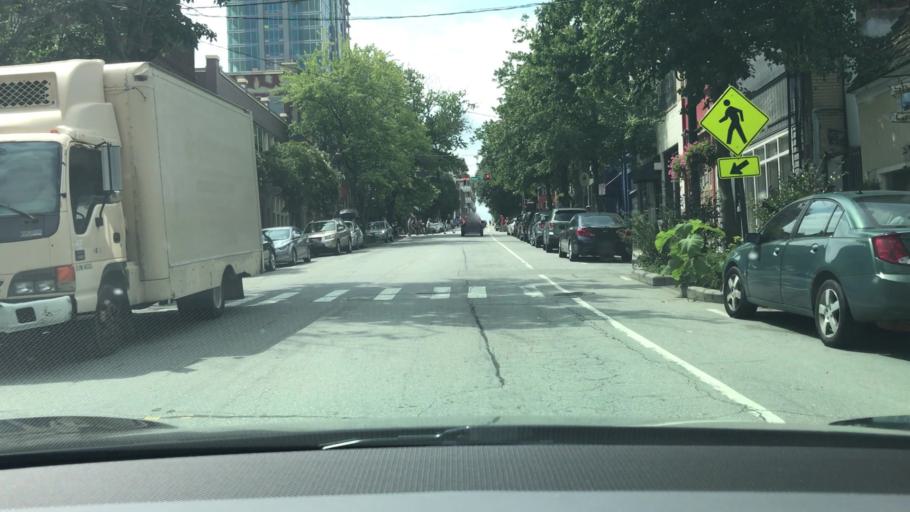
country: US
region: North Carolina
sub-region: Buncombe County
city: Asheville
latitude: 35.5972
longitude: -82.5535
